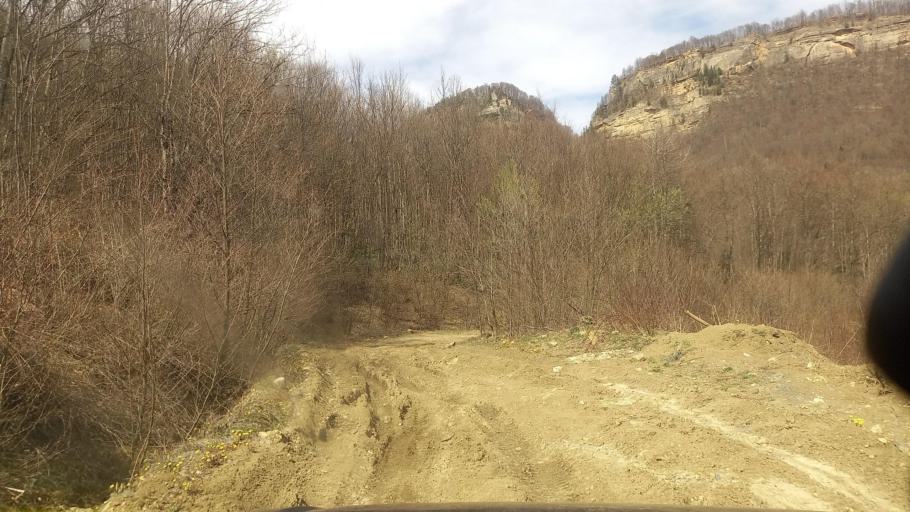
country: RU
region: Adygeya
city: Kamennomostskiy
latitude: 44.1097
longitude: 40.0921
